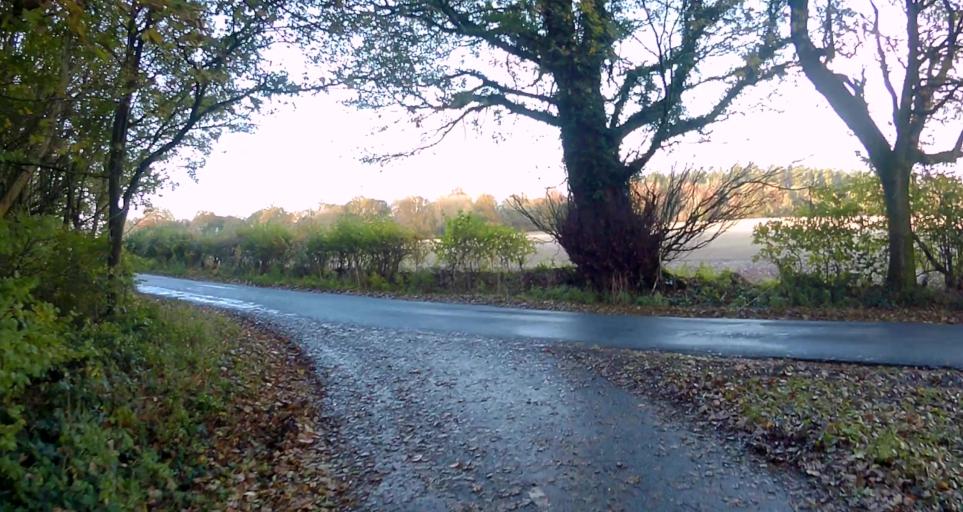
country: GB
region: England
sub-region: Hampshire
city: Basingstoke
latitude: 51.1844
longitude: -1.0711
